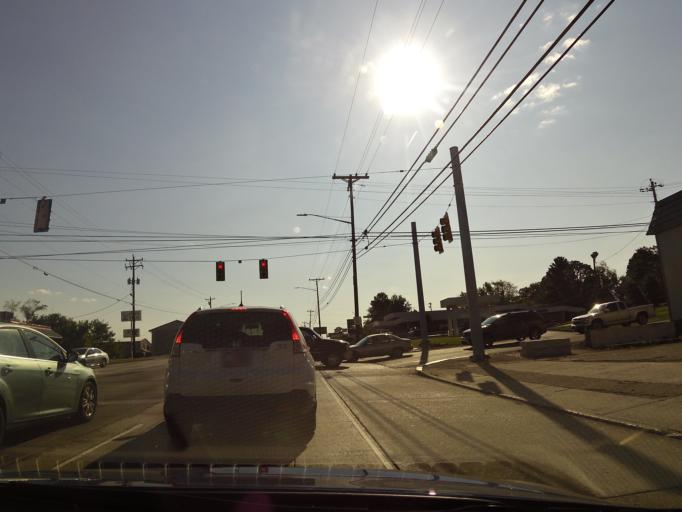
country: US
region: Tennessee
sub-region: Claiborne County
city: New Tazewell
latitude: 36.4428
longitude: -83.5996
